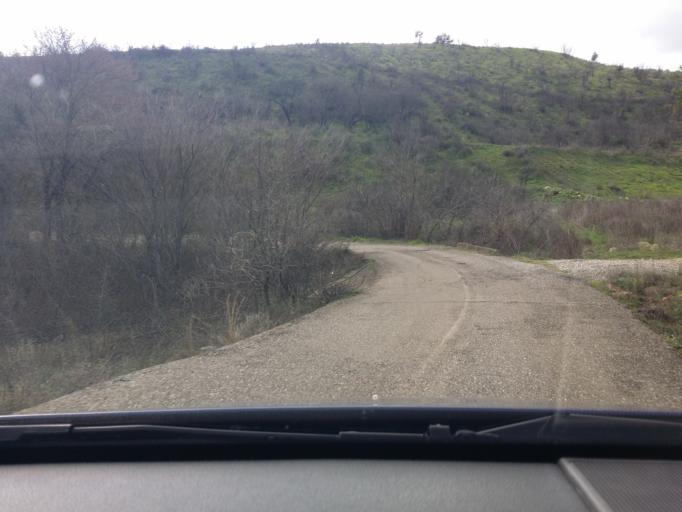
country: GR
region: West Greece
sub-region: Nomos Aitolias kai Akarnanias
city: Fitiai
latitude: 38.6816
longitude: 21.1854
